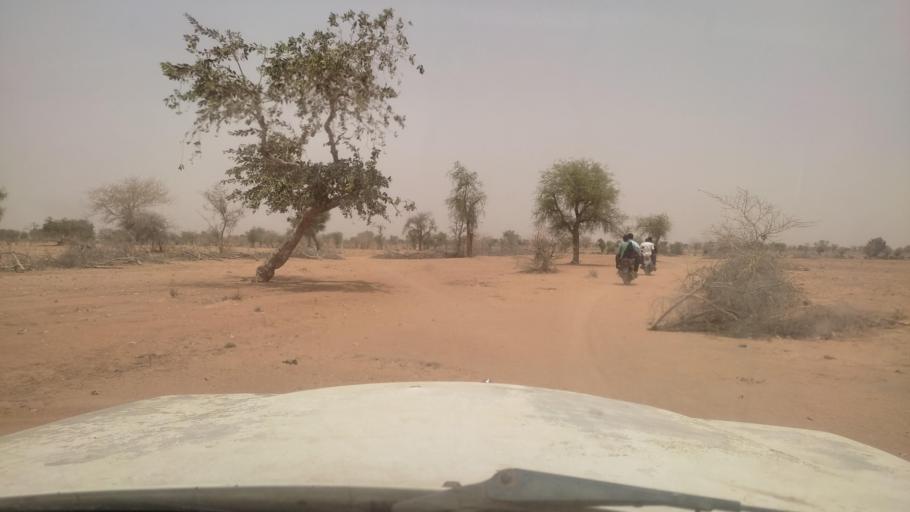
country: BF
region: Est
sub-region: Gnagna Province
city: Bogande
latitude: 13.0372
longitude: -0.0717
